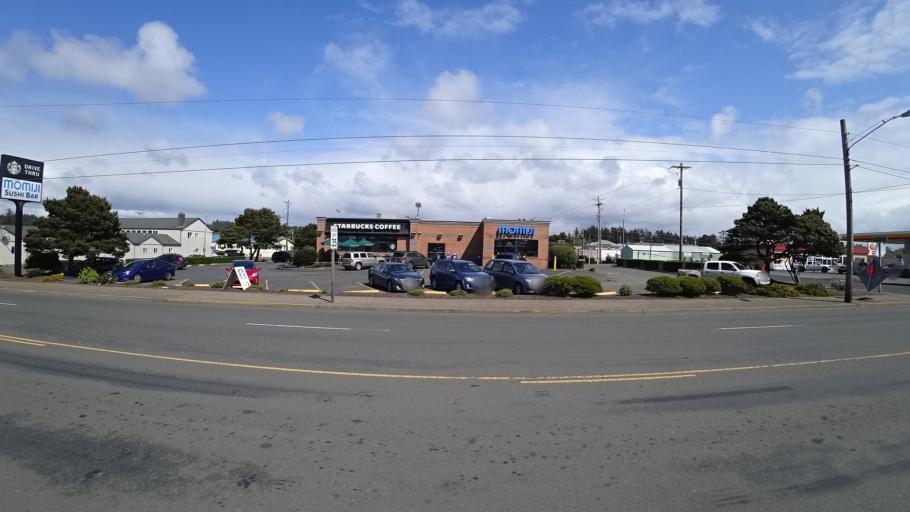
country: US
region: Oregon
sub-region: Lincoln County
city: Newport
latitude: 44.6373
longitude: -124.0532
